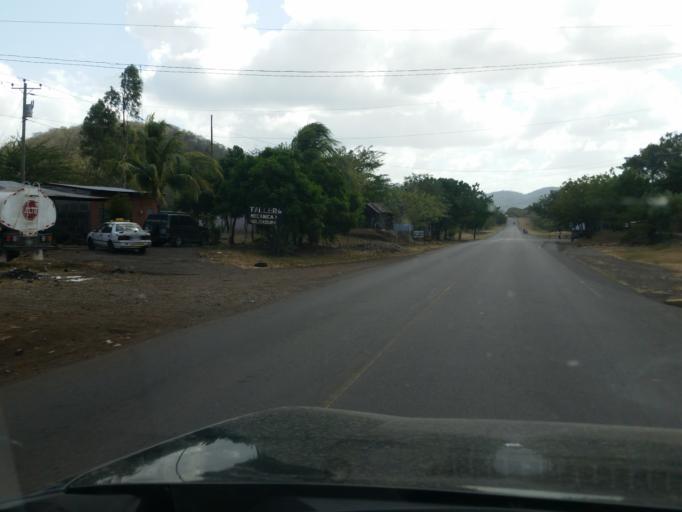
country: NI
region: Chontales
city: Comalapa
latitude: 12.2328
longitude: -85.6456
